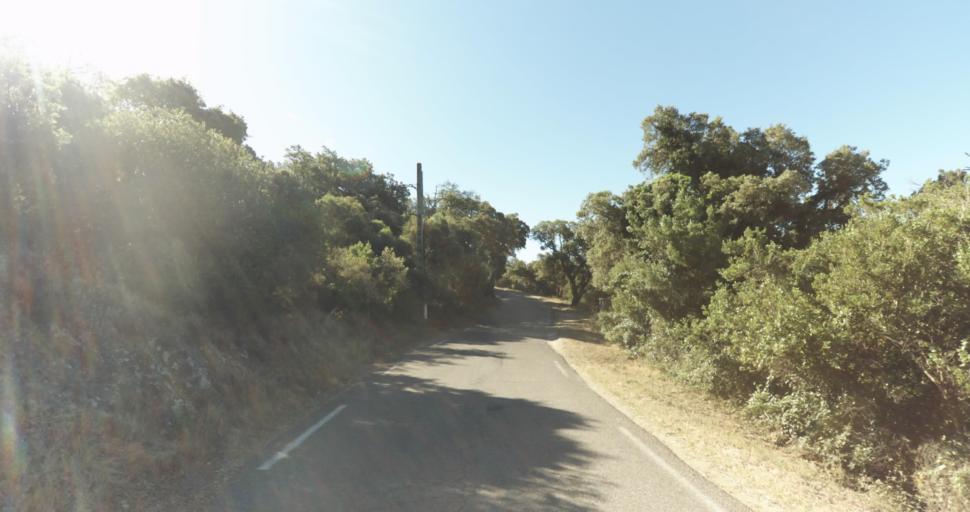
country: FR
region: Provence-Alpes-Cote d'Azur
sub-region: Departement du Var
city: Ramatuelle
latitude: 43.2163
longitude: 6.6013
